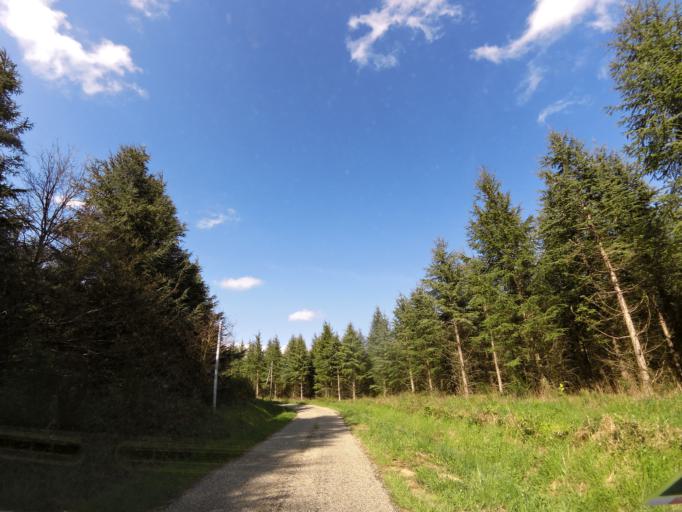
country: FR
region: Midi-Pyrenees
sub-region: Departement du Tarn
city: Soreze
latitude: 43.3796
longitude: 2.0681
